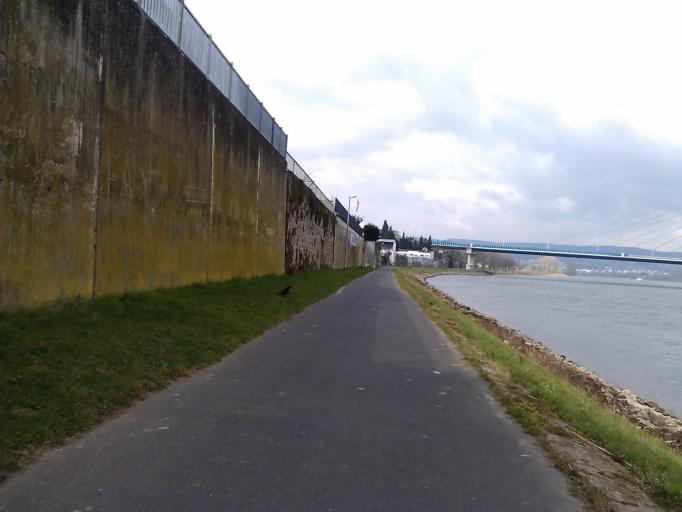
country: DE
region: Rheinland-Pfalz
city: Weissenthurm
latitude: 50.4162
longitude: 7.4593
